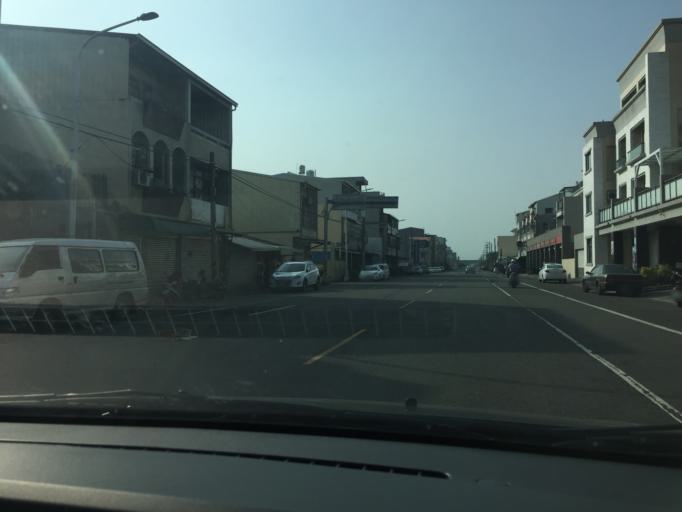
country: TW
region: Taiwan
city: Xinying
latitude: 23.1945
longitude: 120.3065
